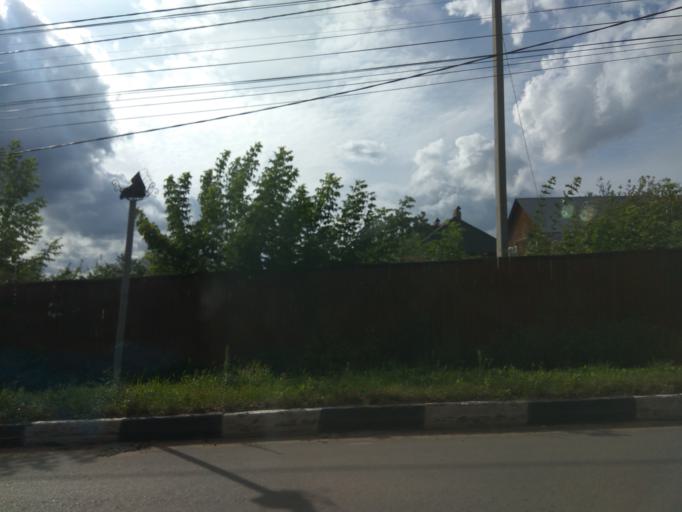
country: RU
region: Moskovskaya
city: Malakhovka
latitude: 55.6411
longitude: 38.0098
